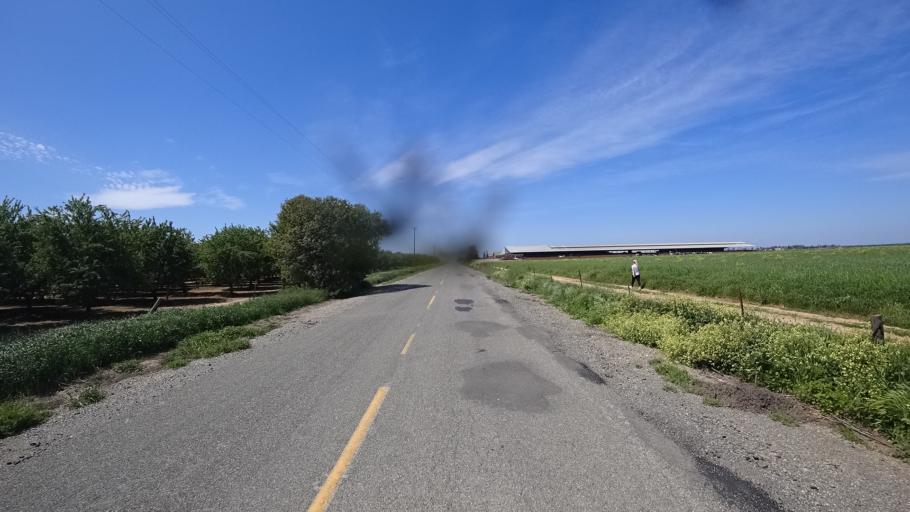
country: US
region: California
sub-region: Glenn County
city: Orland
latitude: 39.6530
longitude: -122.1622
